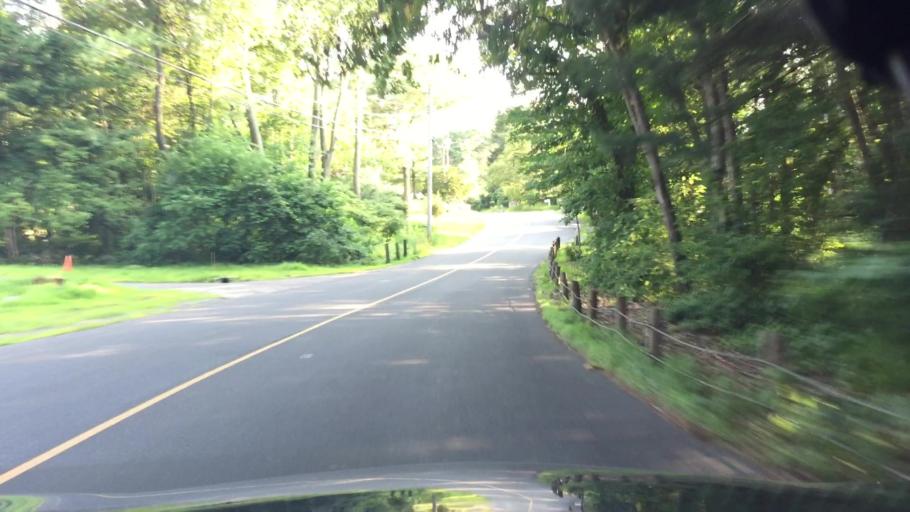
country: US
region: Connecticut
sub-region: New Haven County
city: Woodmont
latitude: 41.2511
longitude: -73.0074
